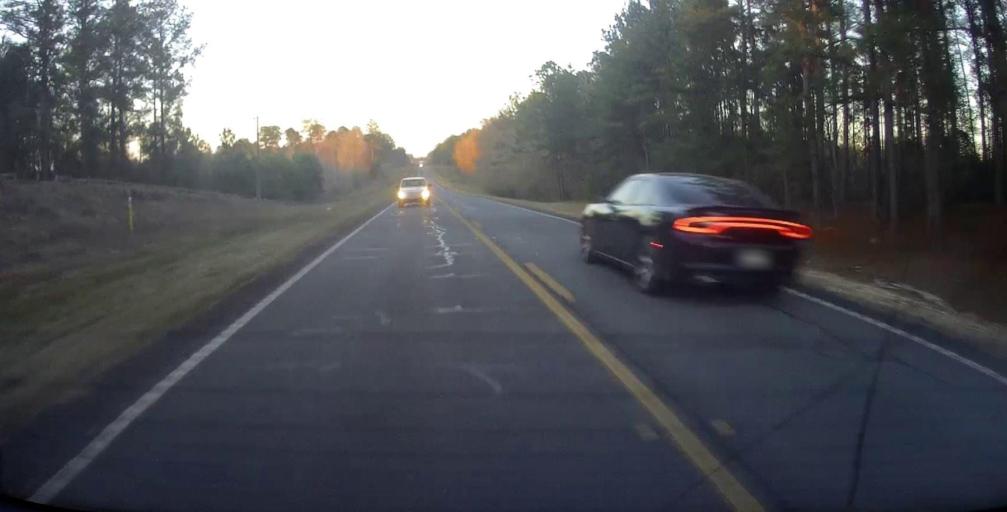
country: US
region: Georgia
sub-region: Dodge County
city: Eastman
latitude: 32.2350
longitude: -83.1498
